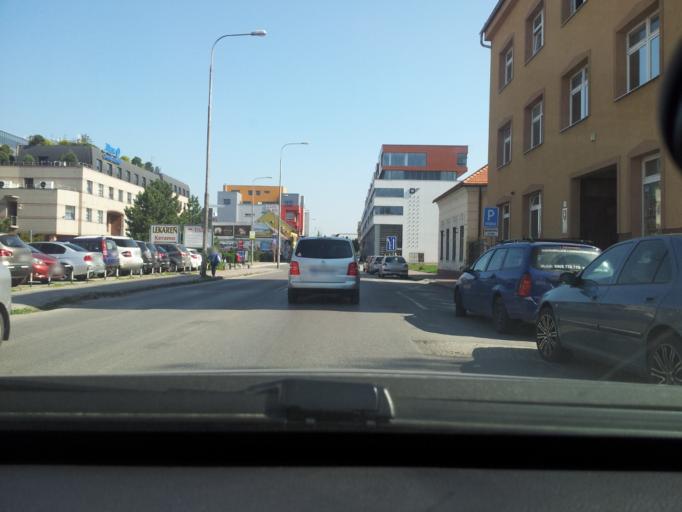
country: SK
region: Trenciansky
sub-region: Okres Trencin
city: Trencin
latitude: 48.8856
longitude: 18.0338
